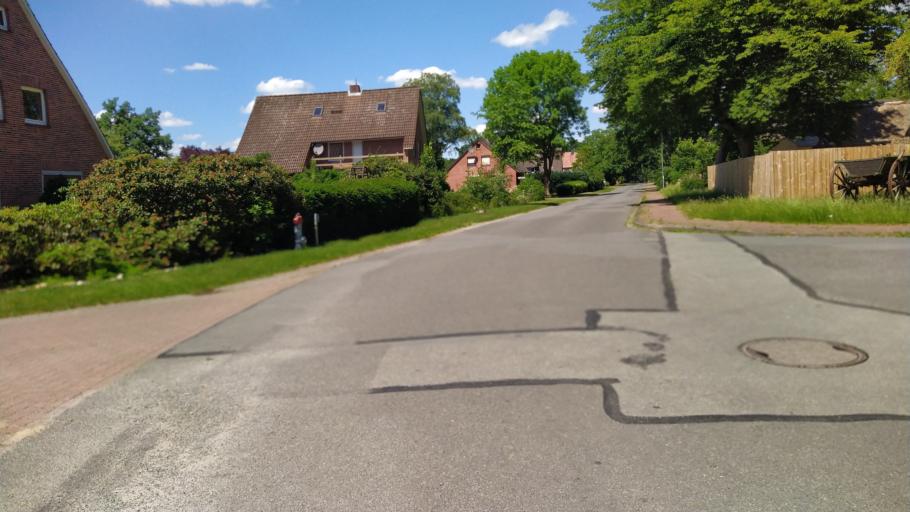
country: DE
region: Lower Saxony
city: Estorf
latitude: 53.5710
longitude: 9.2037
